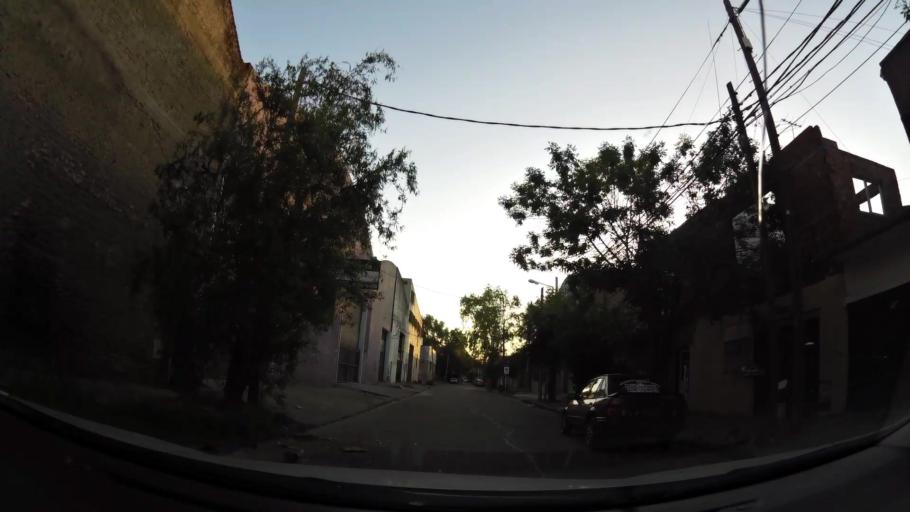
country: AR
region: Buenos Aires
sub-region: Partido de Tigre
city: Tigre
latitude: -34.4418
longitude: -58.5720
